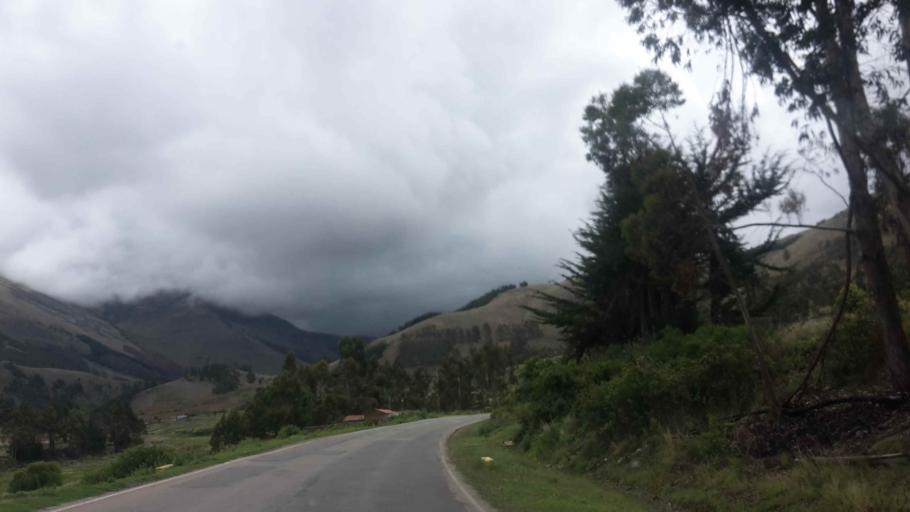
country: BO
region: Cochabamba
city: Arani
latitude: -17.4789
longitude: -65.5388
